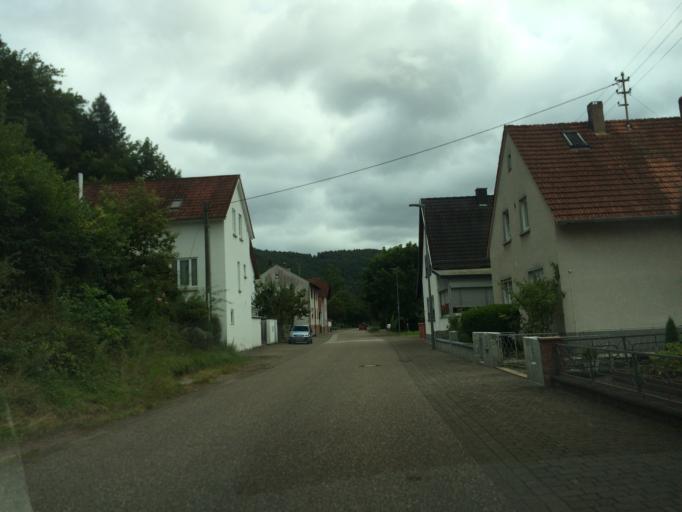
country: DE
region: Rheinland-Pfalz
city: Niederschlettenbach
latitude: 49.0845
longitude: 7.8480
